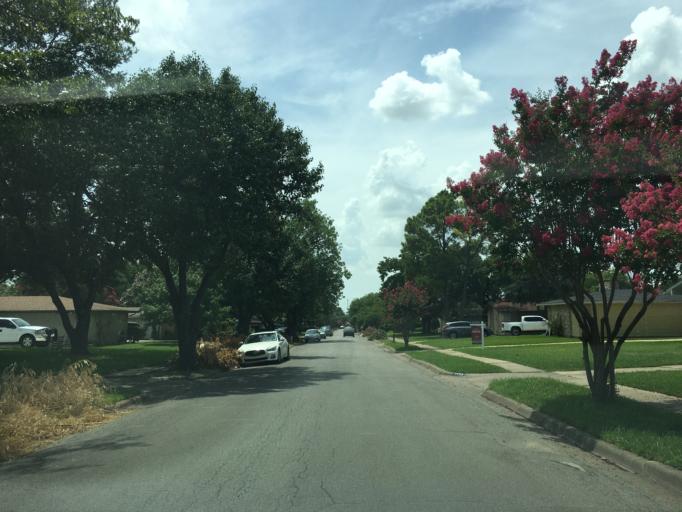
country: US
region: Texas
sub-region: Dallas County
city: Farmers Branch
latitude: 32.9123
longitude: -96.8581
